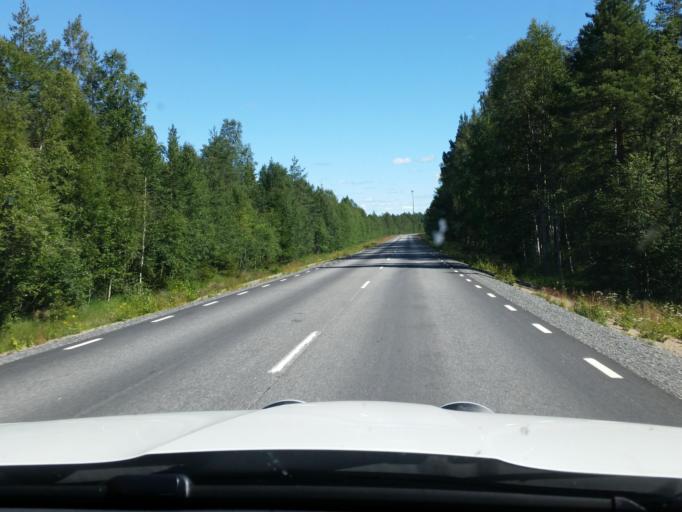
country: SE
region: Vaesterbotten
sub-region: Skelleftea Kommun
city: Storvik
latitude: 65.3388
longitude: 20.9130
